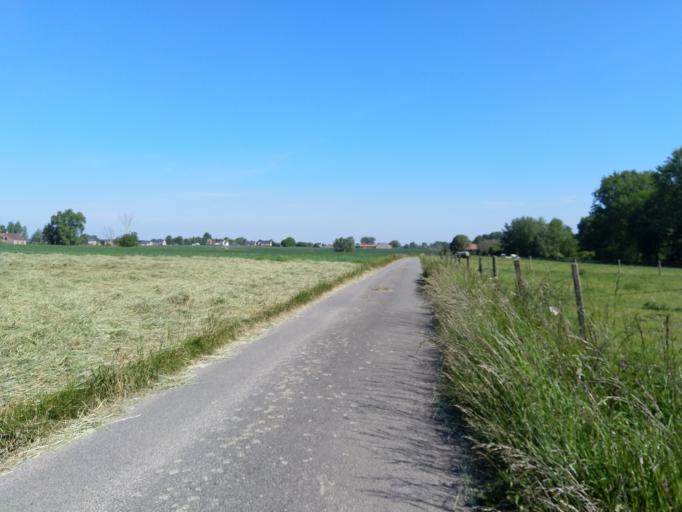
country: BE
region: Wallonia
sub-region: Province du Hainaut
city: Lens
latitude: 50.5433
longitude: 3.8911
